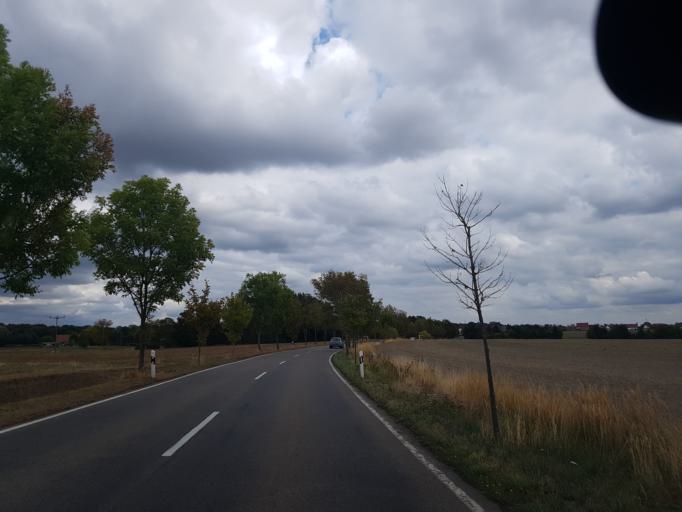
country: DE
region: Saxony-Anhalt
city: Klieken
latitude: 51.9293
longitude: 12.3733
